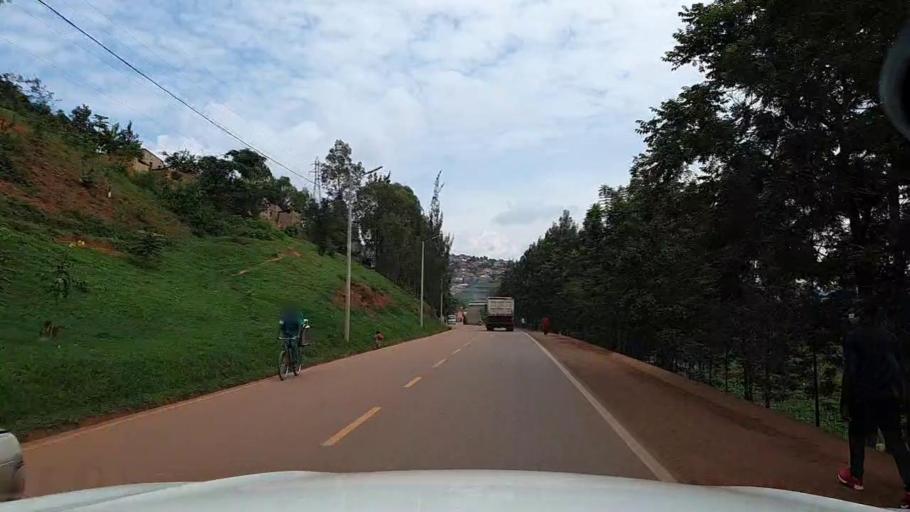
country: RW
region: Kigali
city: Kigali
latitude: -1.9073
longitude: 30.0487
